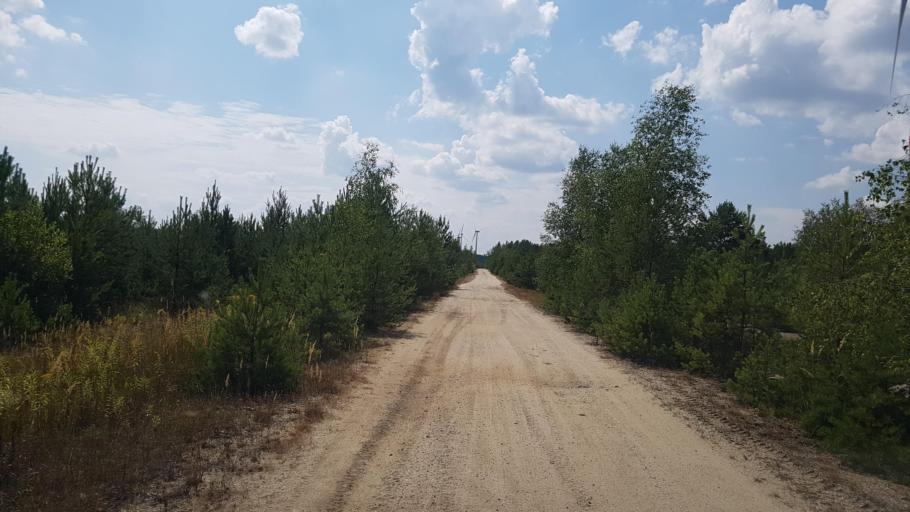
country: DE
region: Brandenburg
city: Sallgast
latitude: 51.5543
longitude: 13.8440
